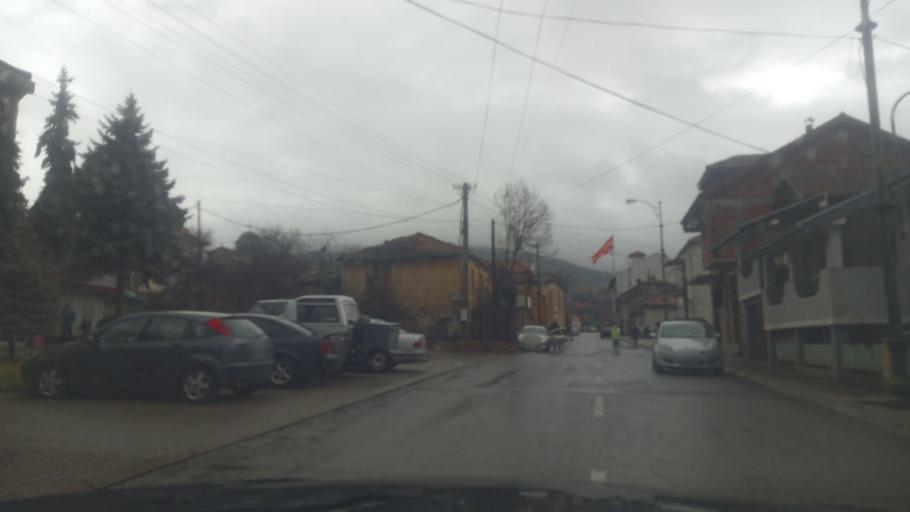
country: MK
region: Pehcevo
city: Pehcevo
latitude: 41.7618
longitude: 22.8850
